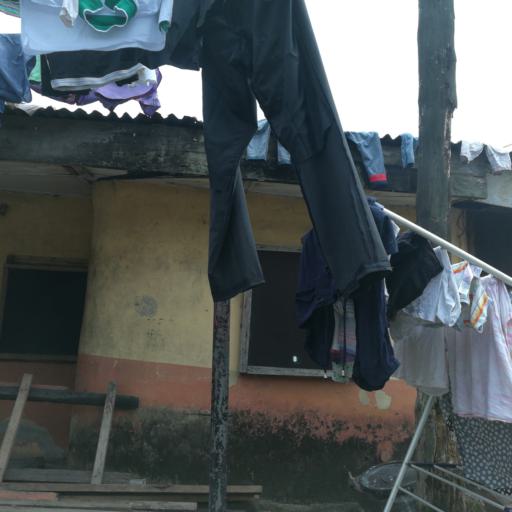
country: NG
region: Rivers
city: Port Harcourt
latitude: 4.7961
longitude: 7.0264
